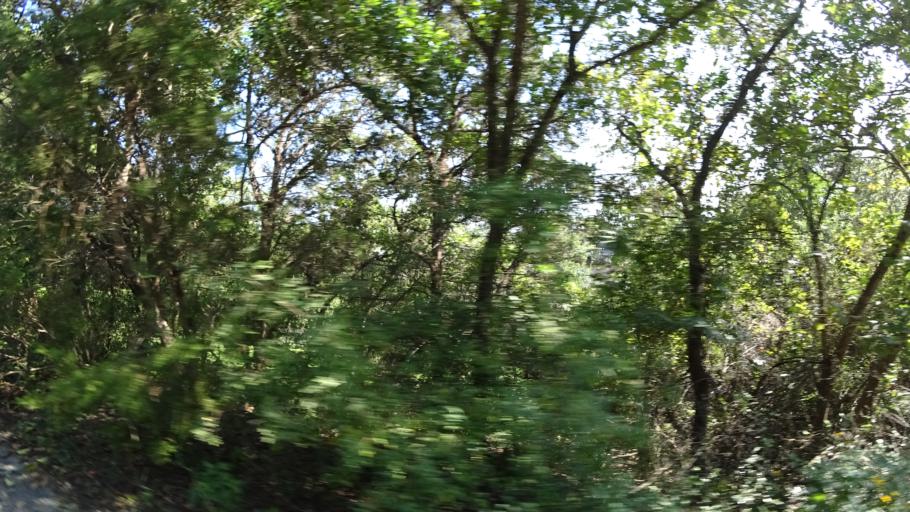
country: US
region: Texas
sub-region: Travis County
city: West Lake Hills
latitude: 30.2900
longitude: -97.8104
